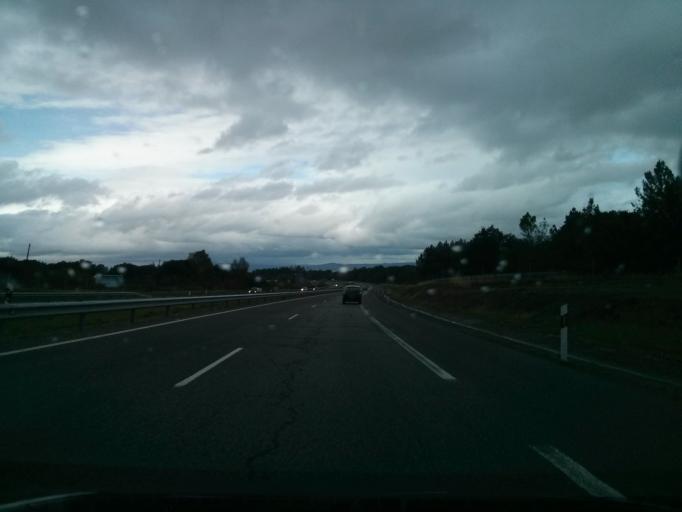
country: ES
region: Galicia
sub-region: Provincia de Ourense
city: Taboadela
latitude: 42.2566
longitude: -7.8687
